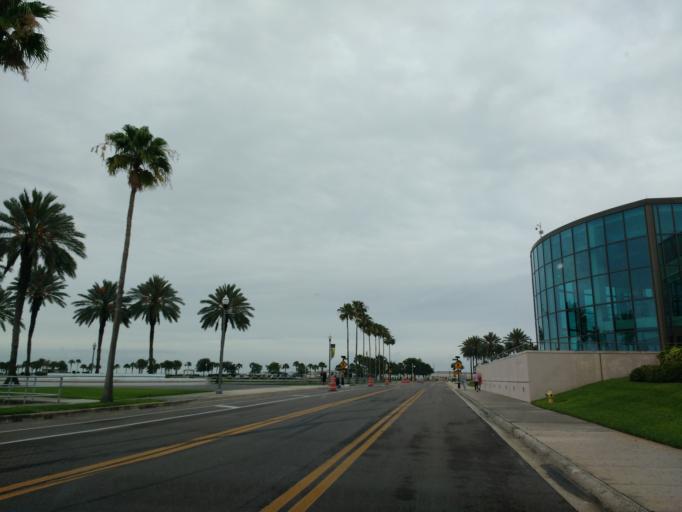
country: US
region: Florida
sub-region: Pinellas County
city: Saint Petersburg
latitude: 27.7675
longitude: -82.6318
